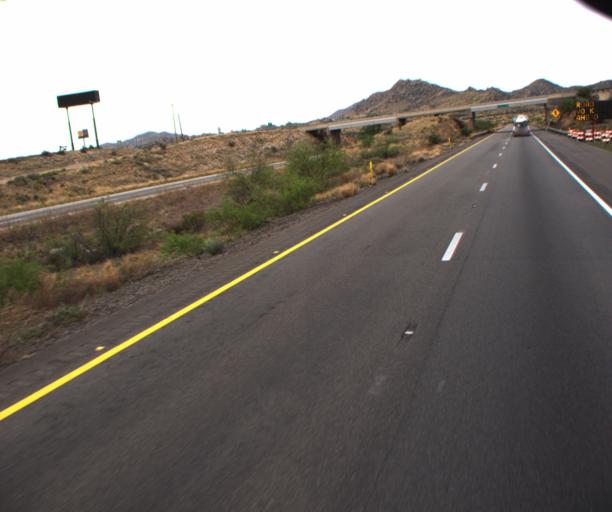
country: US
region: Arizona
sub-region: Cochise County
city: Saint David
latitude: 32.0826
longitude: -110.0504
